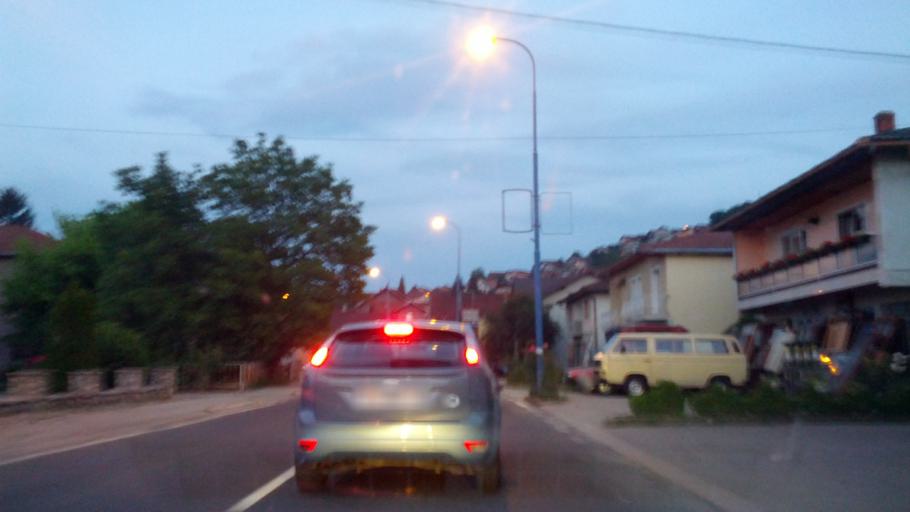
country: BA
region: Federation of Bosnia and Herzegovina
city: Bosanska Krupa
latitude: 44.8799
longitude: 16.1503
